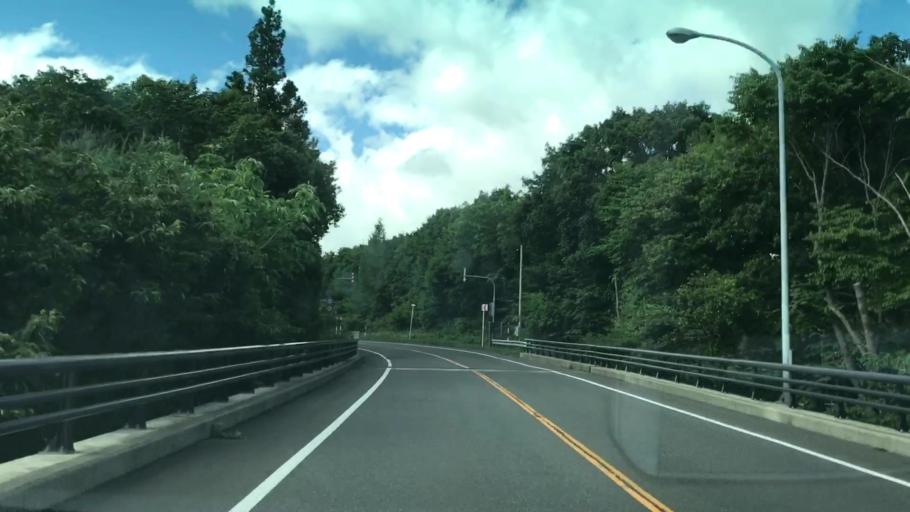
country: JP
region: Hokkaido
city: Muroran
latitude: 42.3797
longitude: 140.9655
